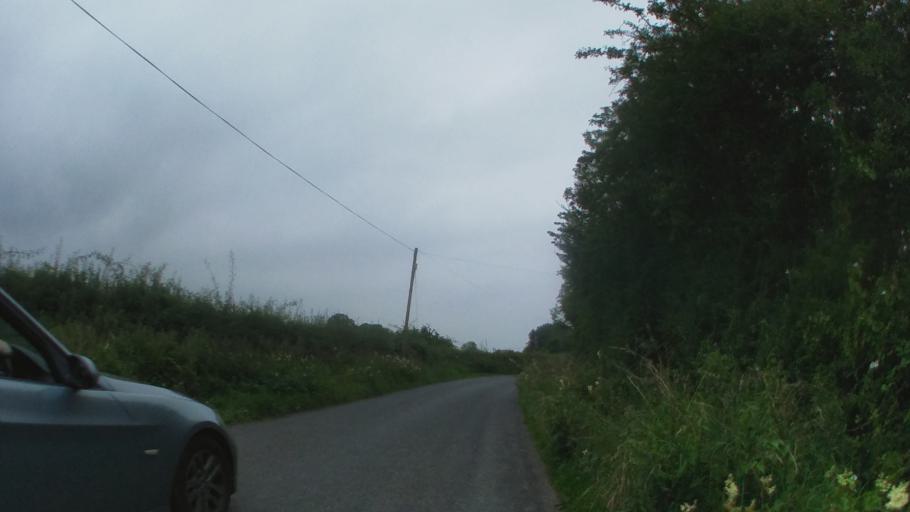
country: IE
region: Leinster
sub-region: Kilkenny
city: Kilkenny
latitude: 52.7008
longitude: -7.1929
